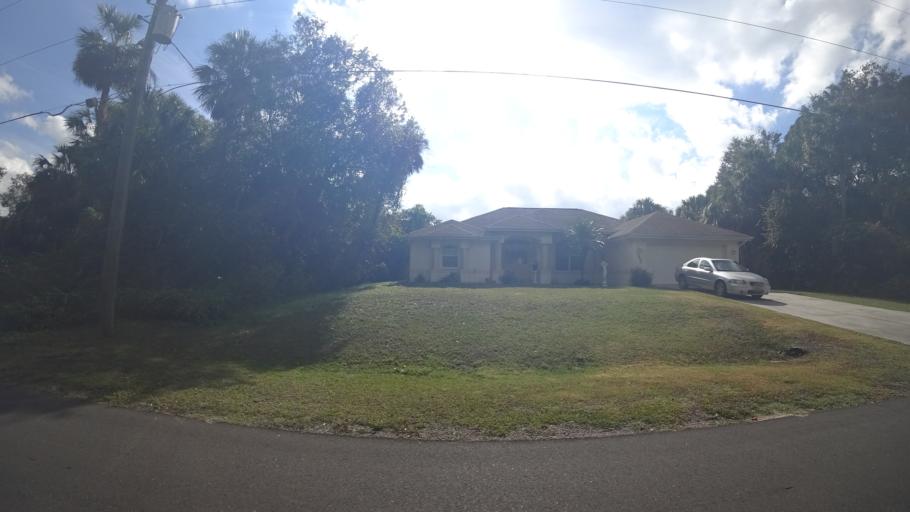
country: US
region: Florida
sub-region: Charlotte County
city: Port Charlotte
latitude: 27.0577
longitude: -82.1191
